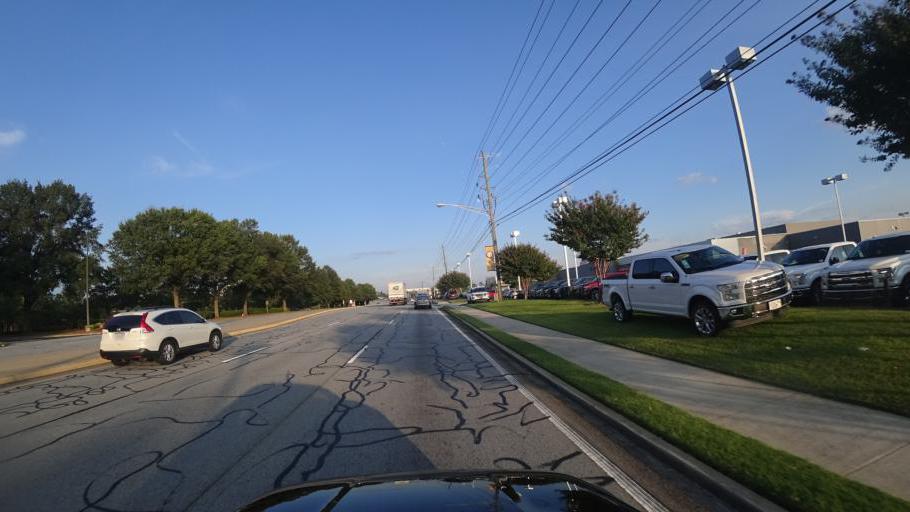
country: US
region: Georgia
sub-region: Gwinnett County
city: Duluth
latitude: 33.9625
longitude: -84.1206
